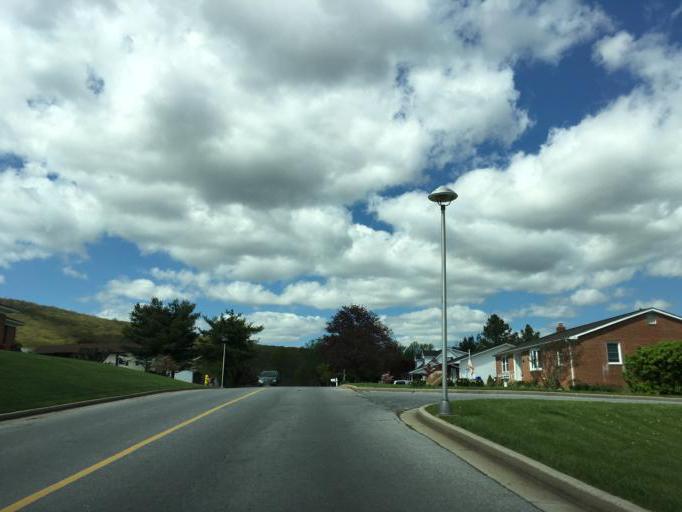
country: US
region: Maryland
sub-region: Frederick County
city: Thurmont
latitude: 39.6186
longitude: -77.4210
